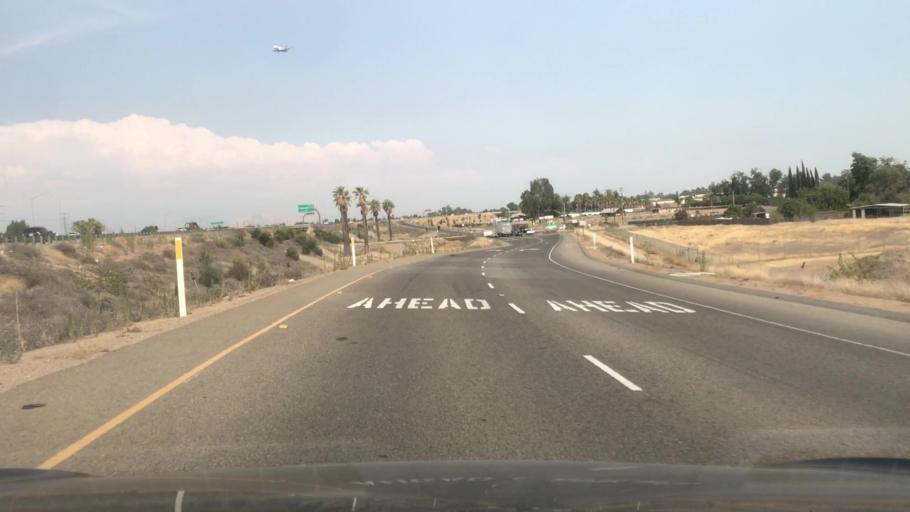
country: US
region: California
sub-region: Fresno County
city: Sunnyside
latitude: 36.7531
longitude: -119.6851
